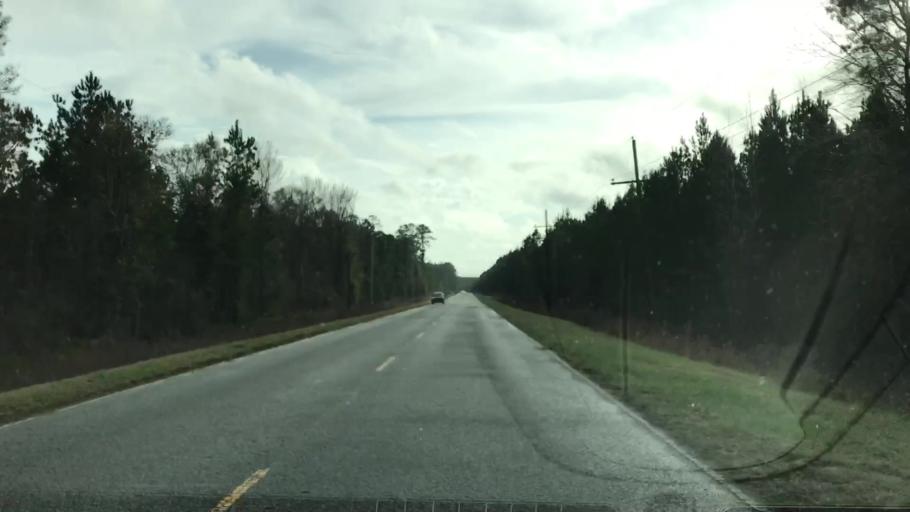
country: US
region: South Carolina
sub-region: Williamsburg County
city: Andrews
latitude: 33.4311
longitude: -79.5937
